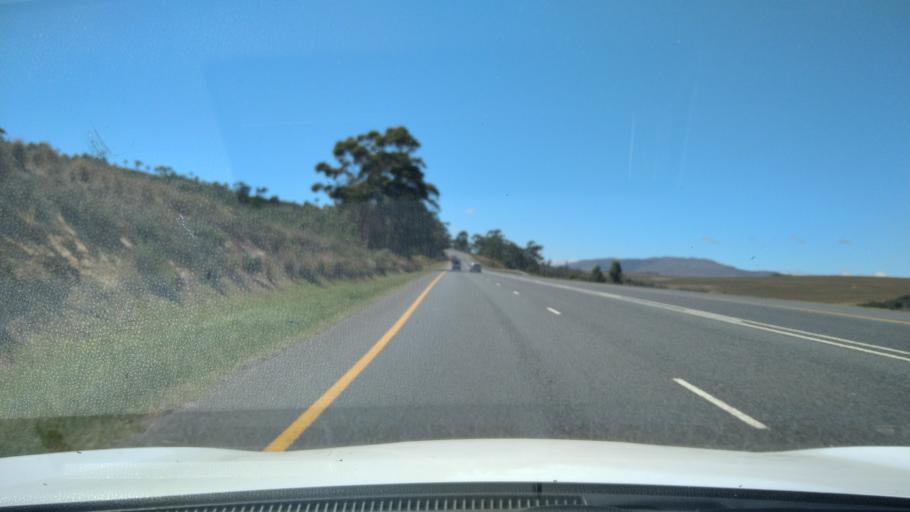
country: ZA
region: Western Cape
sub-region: Overberg District Municipality
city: Caledon
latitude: -34.2163
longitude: 19.4016
